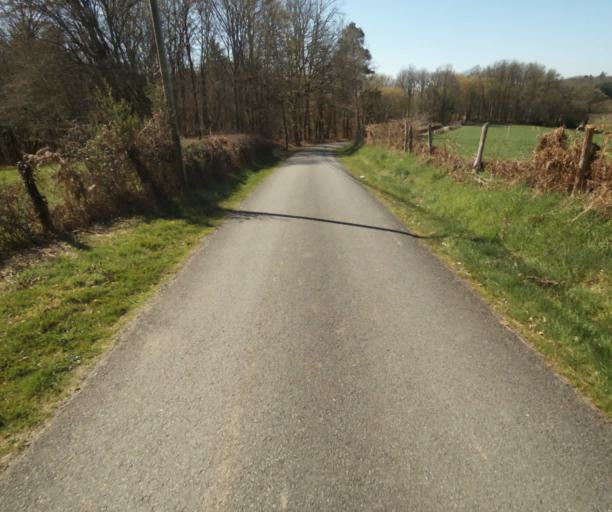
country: FR
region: Limousin
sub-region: Departement de la Correze
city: Saint-Mexant
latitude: 45.3077
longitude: 1.6343
